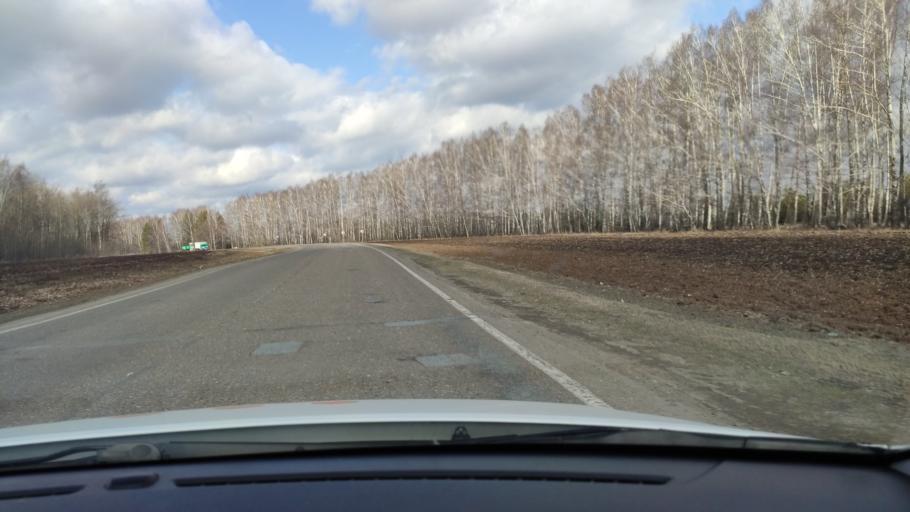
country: RU
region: Tatarstan
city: Vysokaya Gora
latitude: 56.1002
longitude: 49.1819
